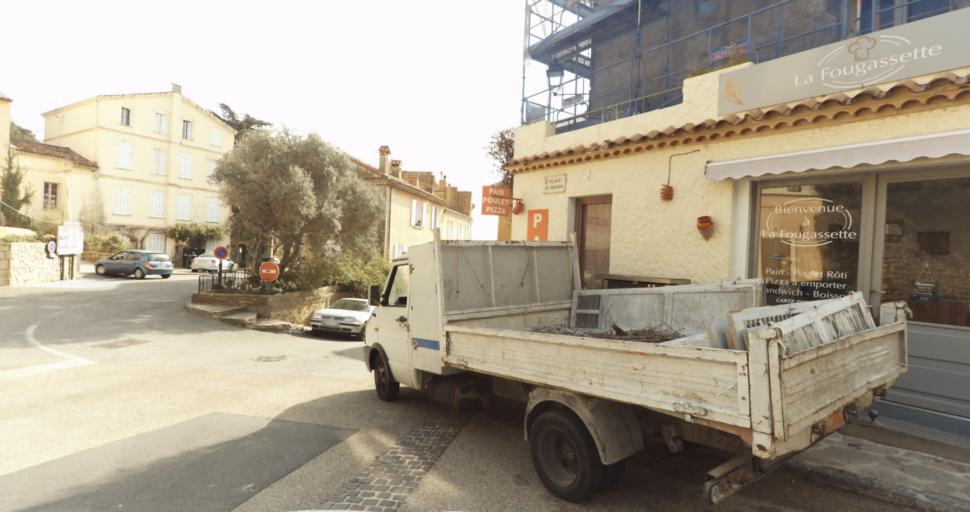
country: FR
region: Provence-Alpes-Cote d'Azur
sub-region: Departement du Var
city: Bormes-les-Mimosas
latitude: 43.1503
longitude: 6.3427
